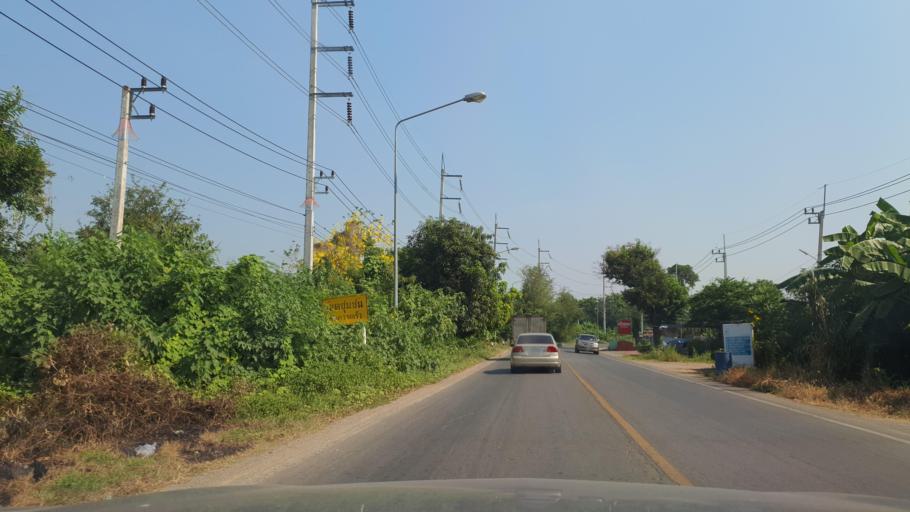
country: TH
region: Kanchanaburi
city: Kanchanaburi
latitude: 14.0461
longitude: 99.4714
